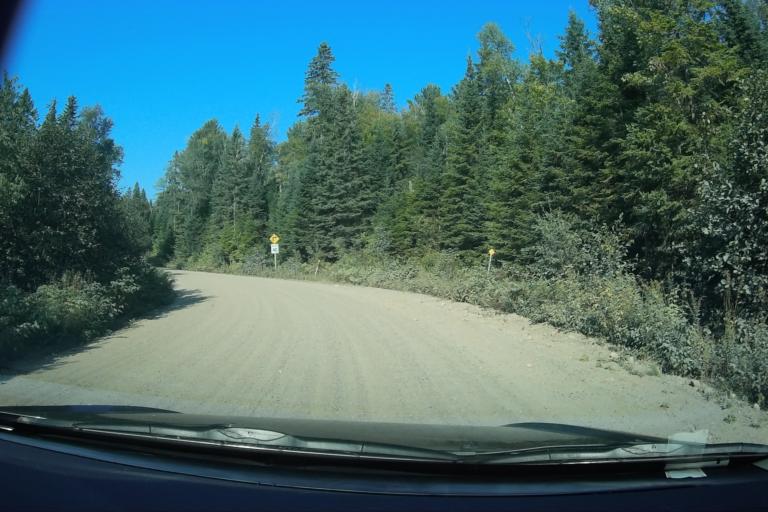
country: CA
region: Ontario
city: Huntsville
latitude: 45.5637
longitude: -78.6991
